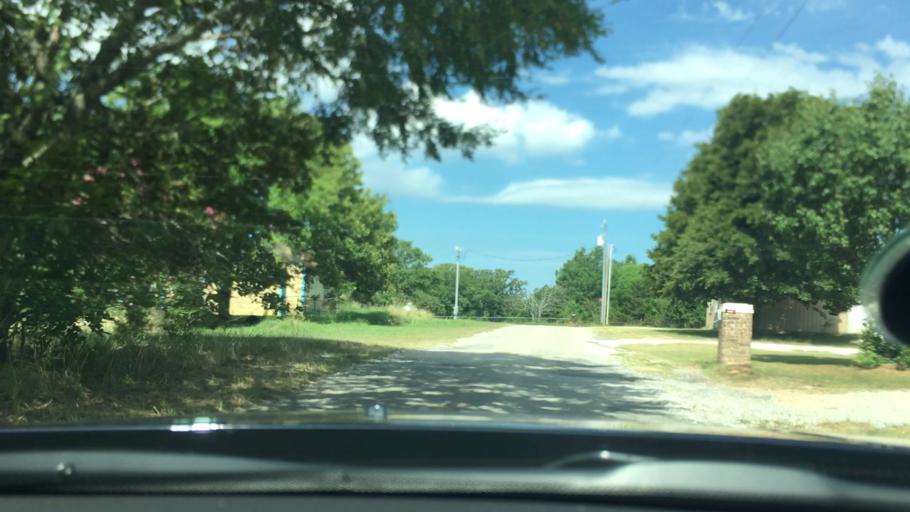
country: US
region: Oklahoma
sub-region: Pontotoc County
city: Ada
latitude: 34.7653
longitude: -96.5639
